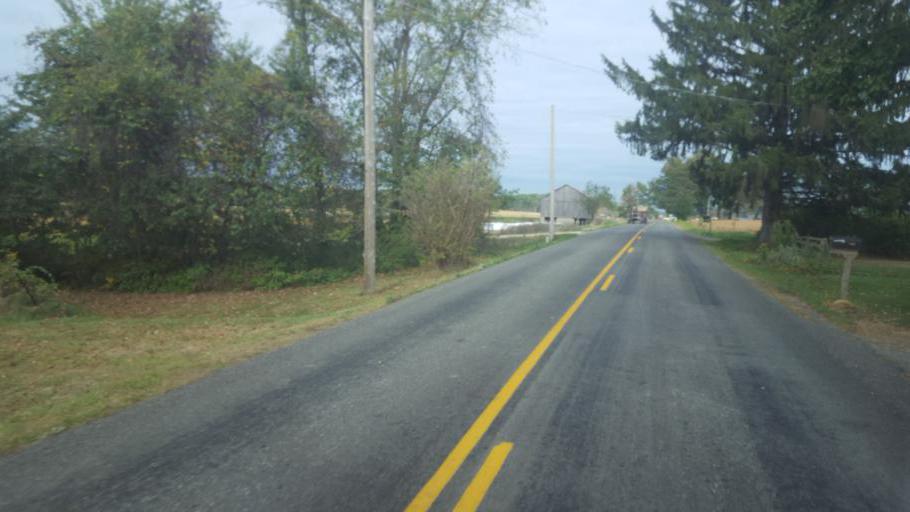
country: US
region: Pennsylvania
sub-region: Mercer County
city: Reynolds Heights
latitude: 41.3431
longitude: -80.2783
